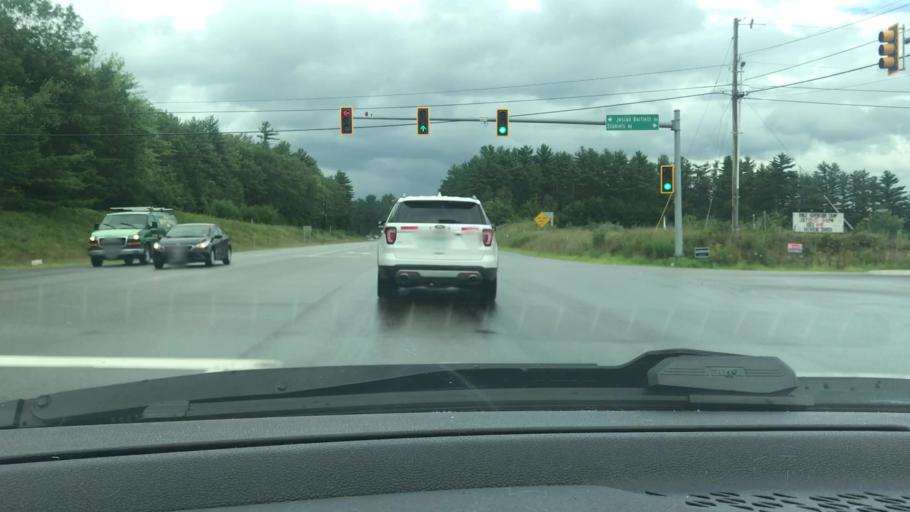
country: US
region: New Hampshire
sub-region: Merrimack County
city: Chichester
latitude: 43.2536
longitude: -71.4590
